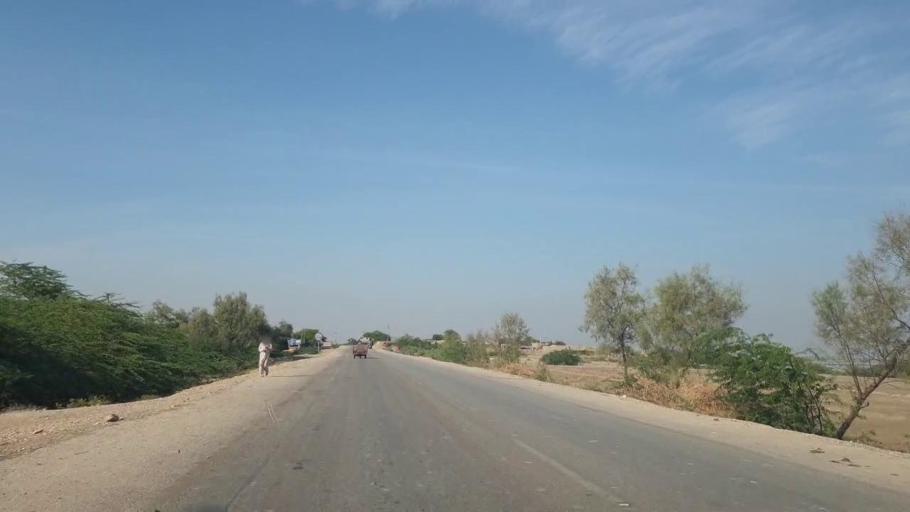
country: PK
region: Sindh
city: Sehwan
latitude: 26.3834
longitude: 67.8714
